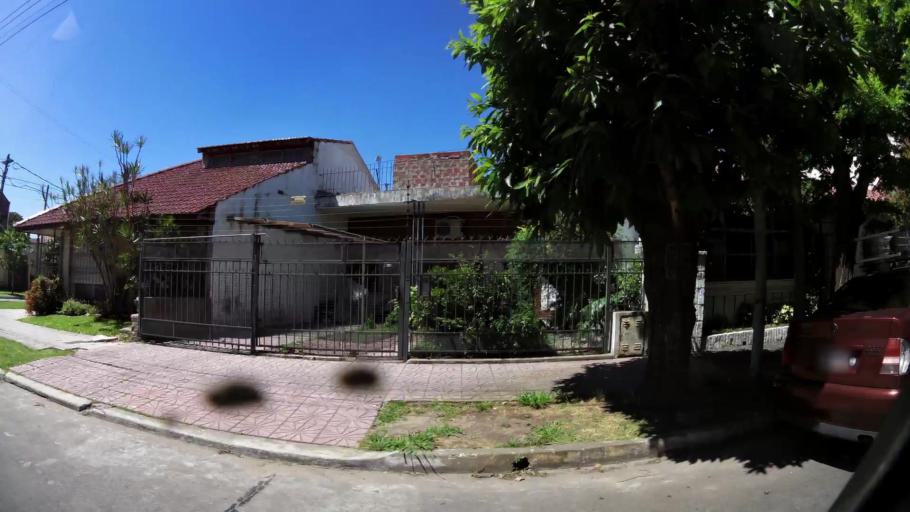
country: AR
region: Buenos Aires
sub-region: Partido de Quilmes
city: Quilmes
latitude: -34.7149
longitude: -58.2787
